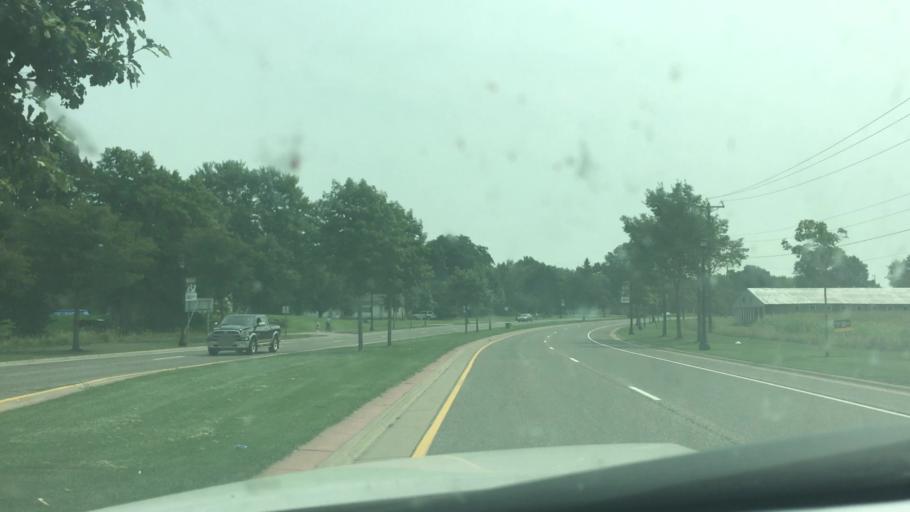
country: US
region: Minnesota
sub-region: Washington County
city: Hugo
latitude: 45.1643
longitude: -93.0070
